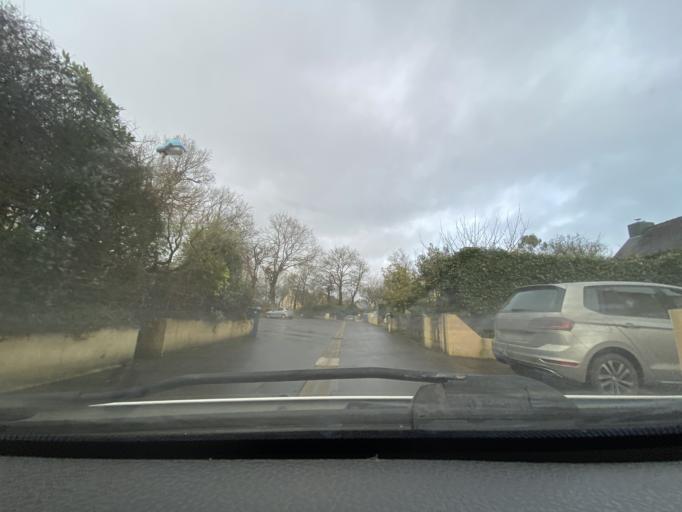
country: FR
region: Brittany
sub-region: Departement d'Ille-et-Vilaine
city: Melesse
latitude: 48.2225
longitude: -1.6956
